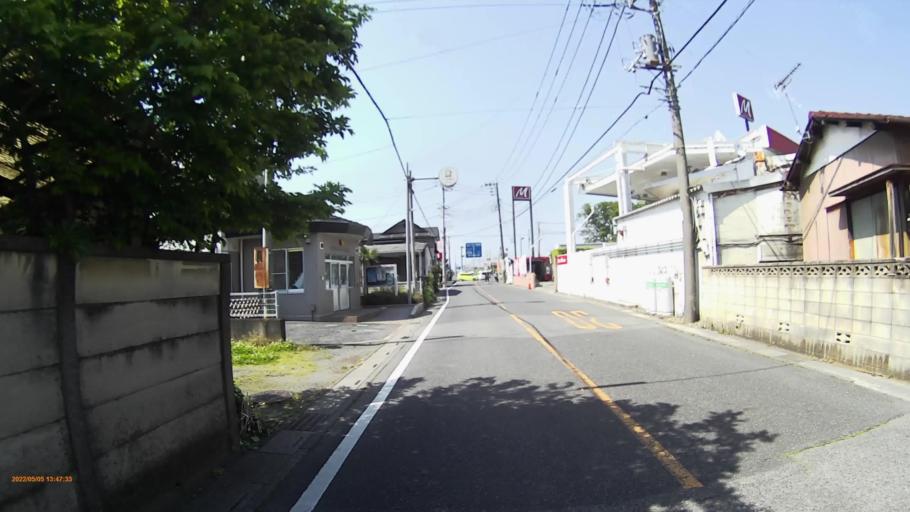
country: JP
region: Saitama
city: Kasukabe
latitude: 35.9903
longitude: 139.7530
